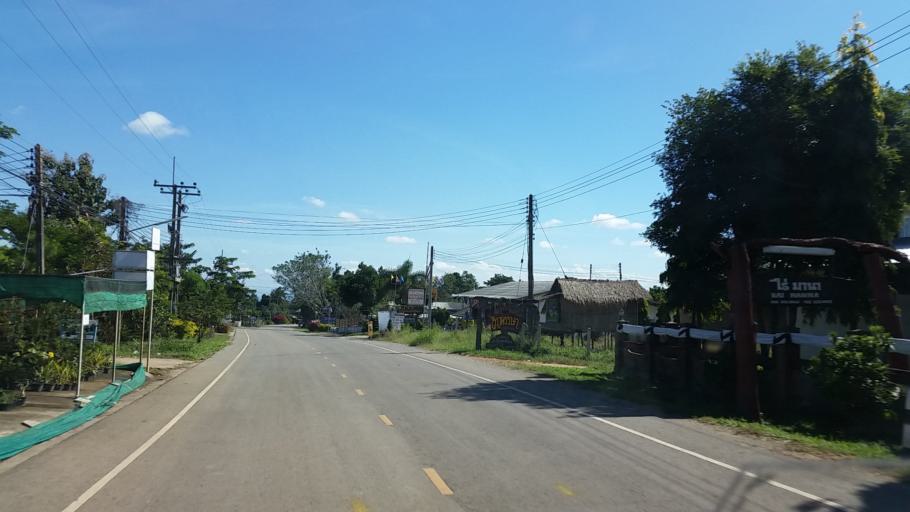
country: TH
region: Chaiyaphum
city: Sap Yai
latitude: 15.6264
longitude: 101.3981
